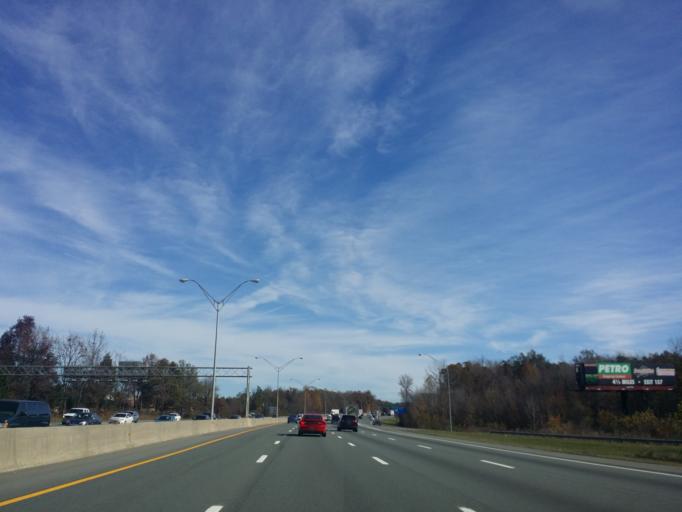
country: US
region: North Carolina
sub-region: Alamance County
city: Mebane
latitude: 36.0676
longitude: -79.3092
